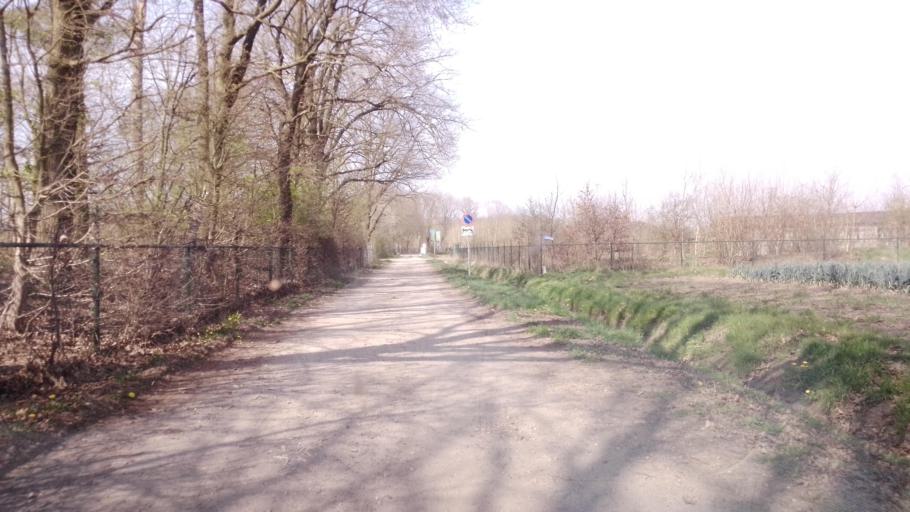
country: NL
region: Limburg
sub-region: Gemeente Peel en Maas
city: Maasbree
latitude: 51.3786
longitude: 6.0657
